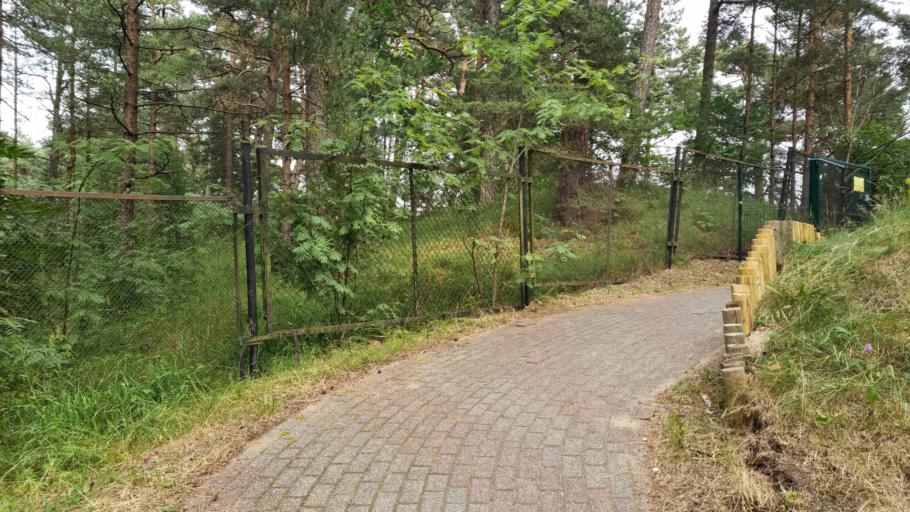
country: LV
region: Ventspils
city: Ventspils
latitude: 57.3850
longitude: 21.5330
